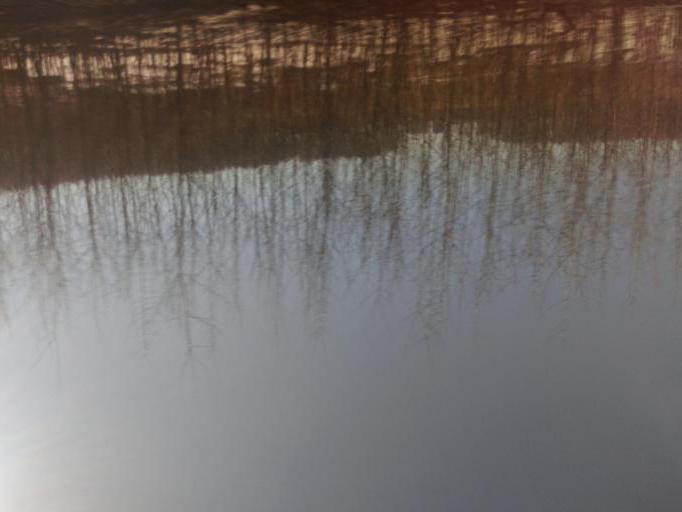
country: RU
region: Moskovskaya
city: Kommunarka
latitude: 55.5373
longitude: 37.4704
